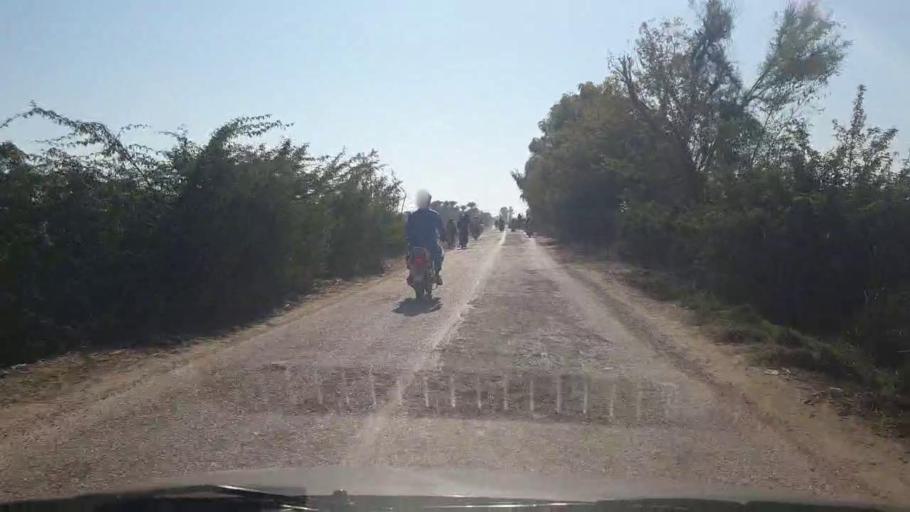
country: PK
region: Sindh
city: Bozdar
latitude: 27.1729
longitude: 68.6413
